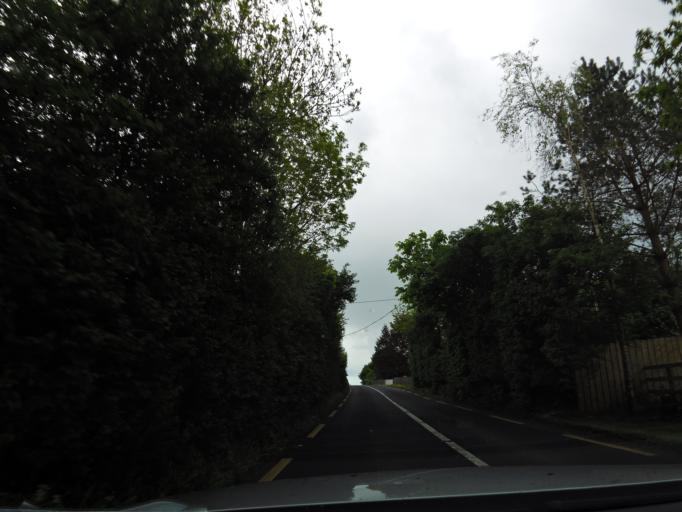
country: IE
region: Munster
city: Thurles
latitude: 52.6974
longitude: -7.8182
